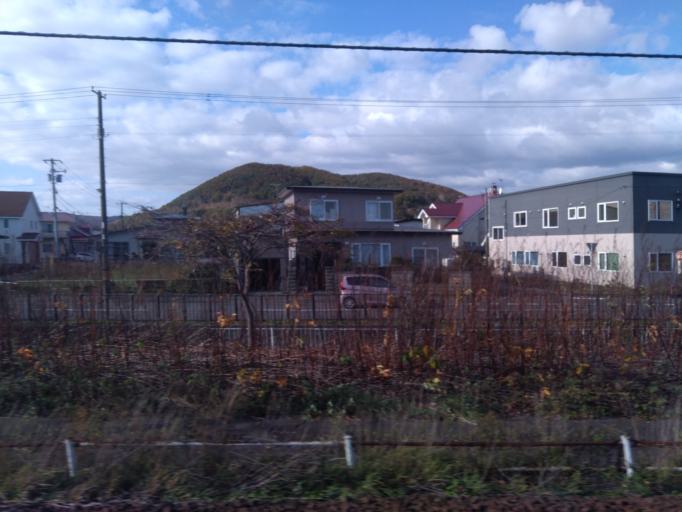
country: JP
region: Hokkaido
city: Muroran
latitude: 42.3635
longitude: 141.0506
